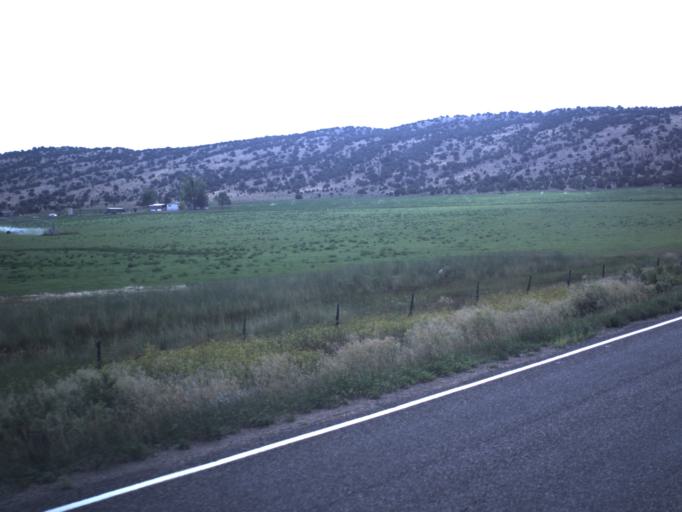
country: US
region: Utah
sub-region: Daggett County
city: Manila
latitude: 40.9485
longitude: -109.7114
